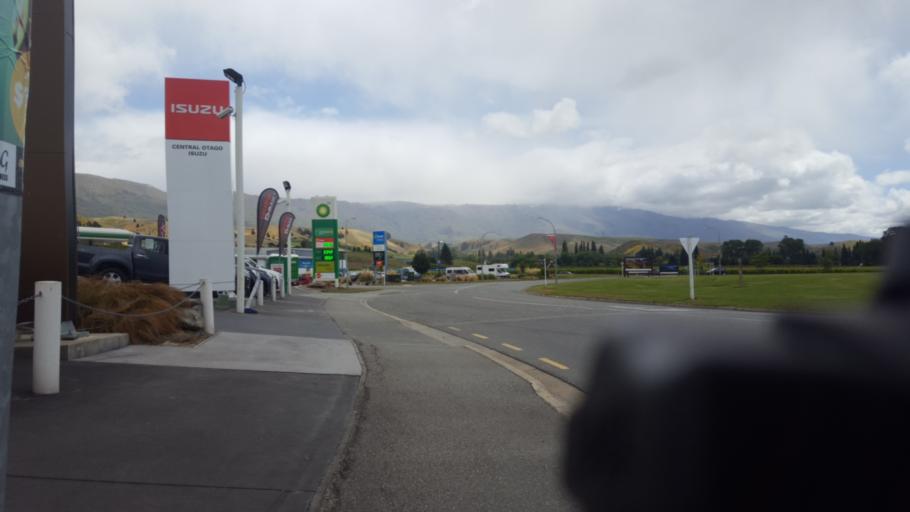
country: NZ
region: Otago
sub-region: Queenstown-Lakes District
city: Wanaka
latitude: -45.0367
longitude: 169.1948
